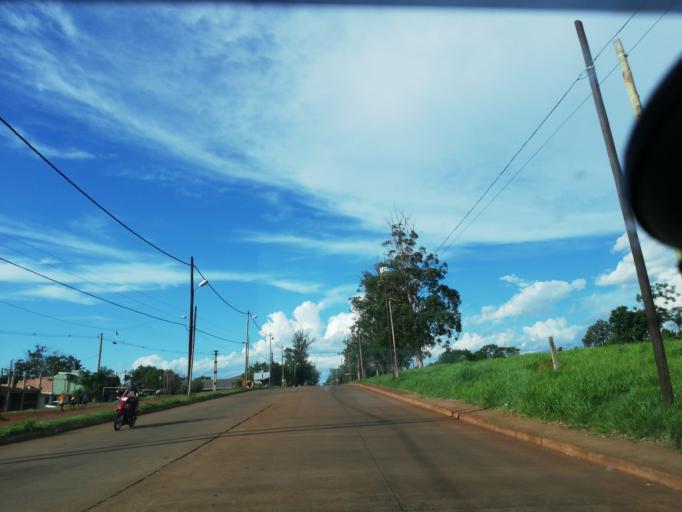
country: AR
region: Misiones
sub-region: Departamento de Capital
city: Posadas
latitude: -27.4106
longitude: -55.9549
